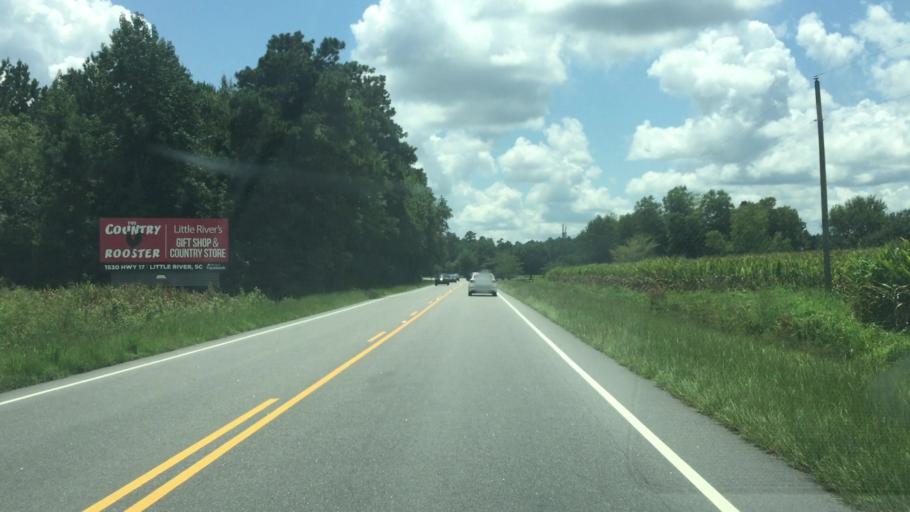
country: US
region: North Carolina
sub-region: Columbus County
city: Tabor City
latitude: 34.1853
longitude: -78.8379
